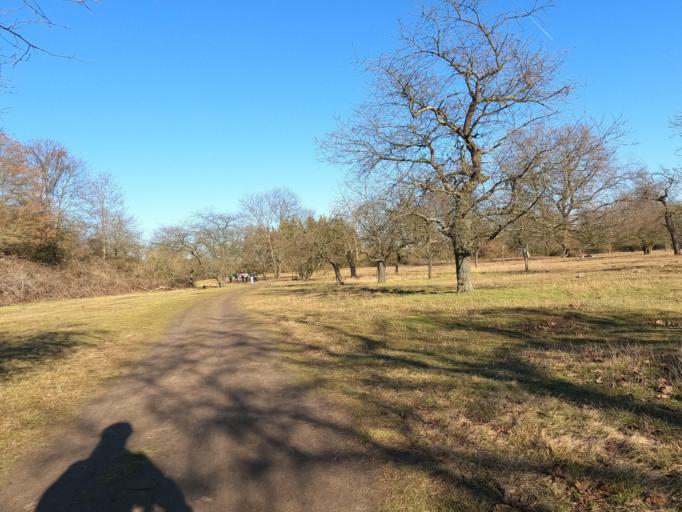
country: DE
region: Hesse
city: Kelsterbach
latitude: 50.0847
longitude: 8.5562
